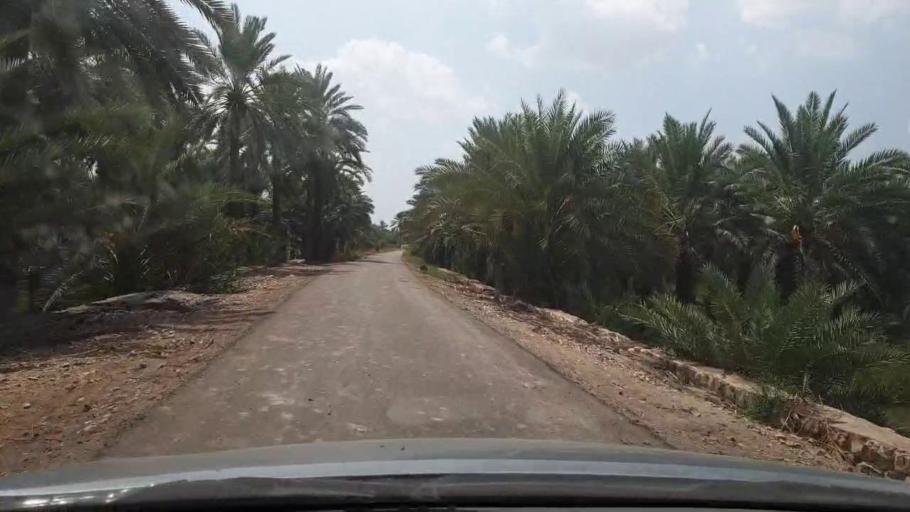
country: PK
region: Sindh
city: Kot Diji
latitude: 27.3976
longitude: 68.7416
